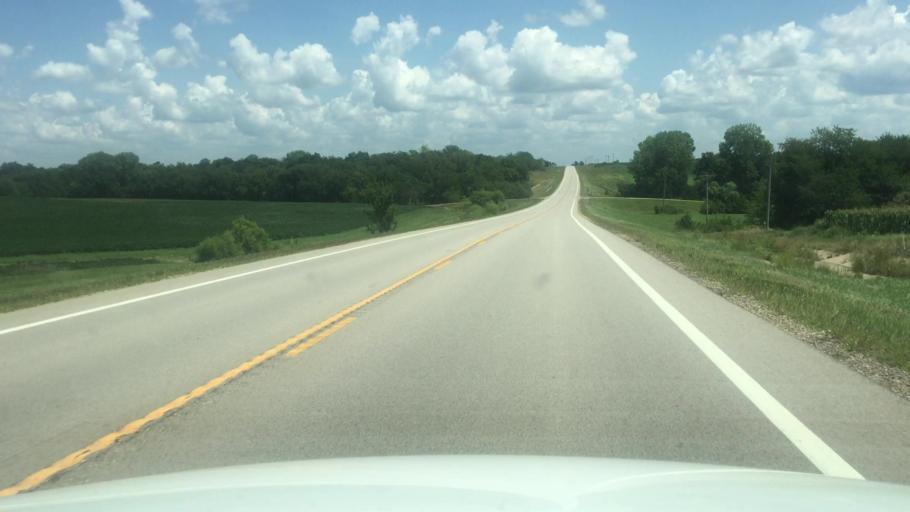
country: US
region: Kansas
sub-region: Brown County
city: Horton
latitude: 39.6673
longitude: -95.4553
